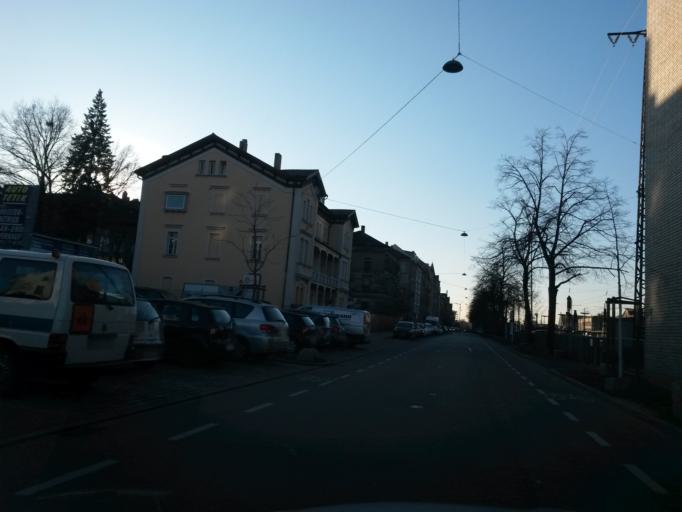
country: DE
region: Bavaria
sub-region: Regierungsbezirk Mittelfranken
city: Furth
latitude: 49.4685
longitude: 10.9937
